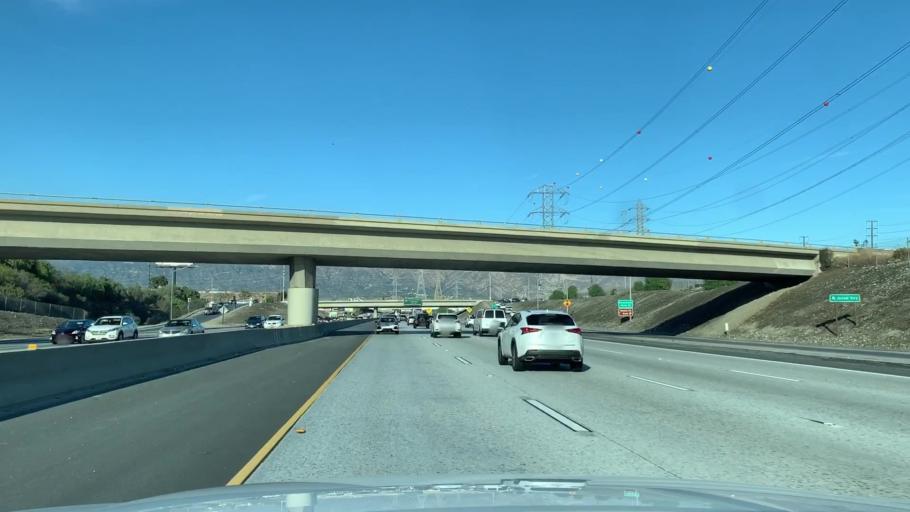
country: US
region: California
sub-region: Los Angeles County
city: Mayflower Village
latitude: 34.1061
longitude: -117.9826
